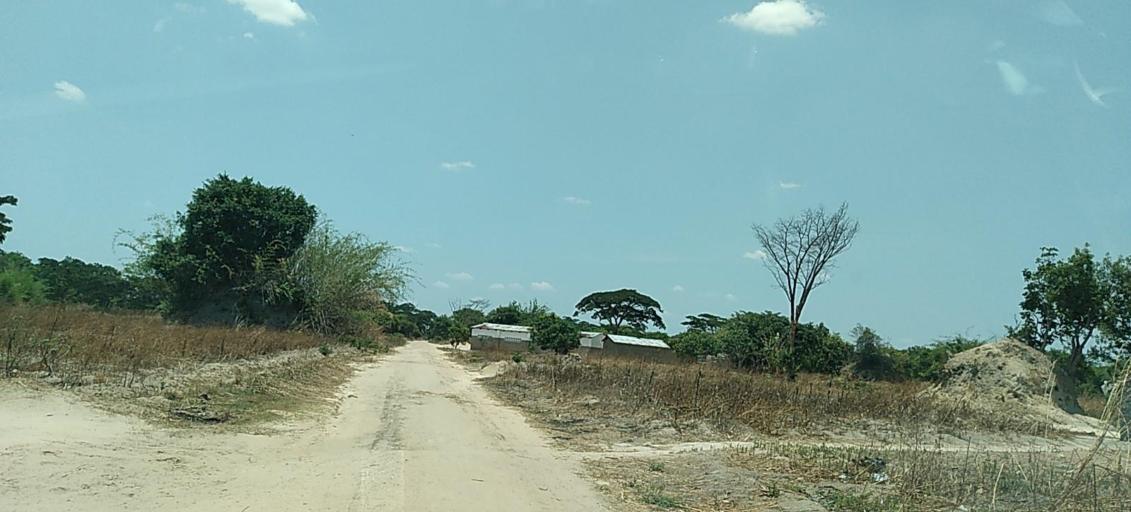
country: ZM
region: Copperbelt
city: Luanshya
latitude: -13.0763
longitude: 28.4050
